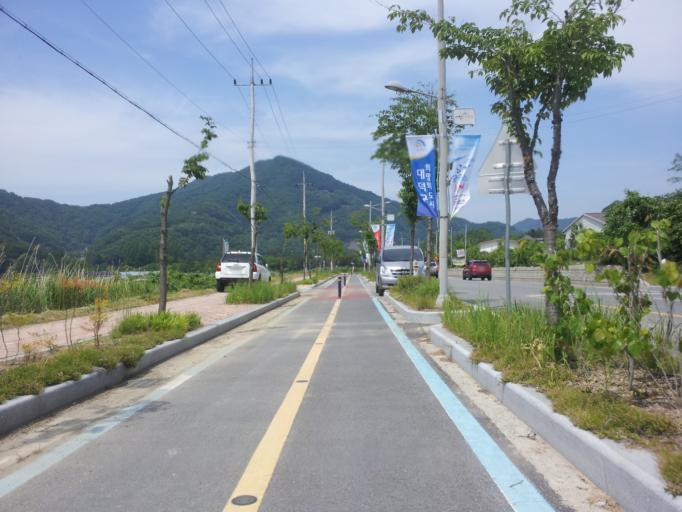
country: KR
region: Daejeon
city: Sintansin
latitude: 36.4680
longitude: 127.4701
